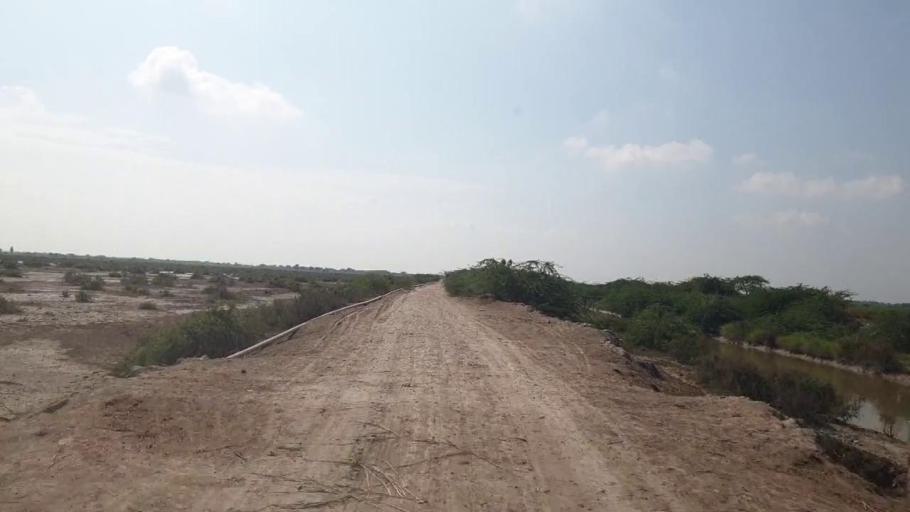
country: PK
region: Sindh
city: Badin
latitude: 24.5009
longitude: 68.6073
